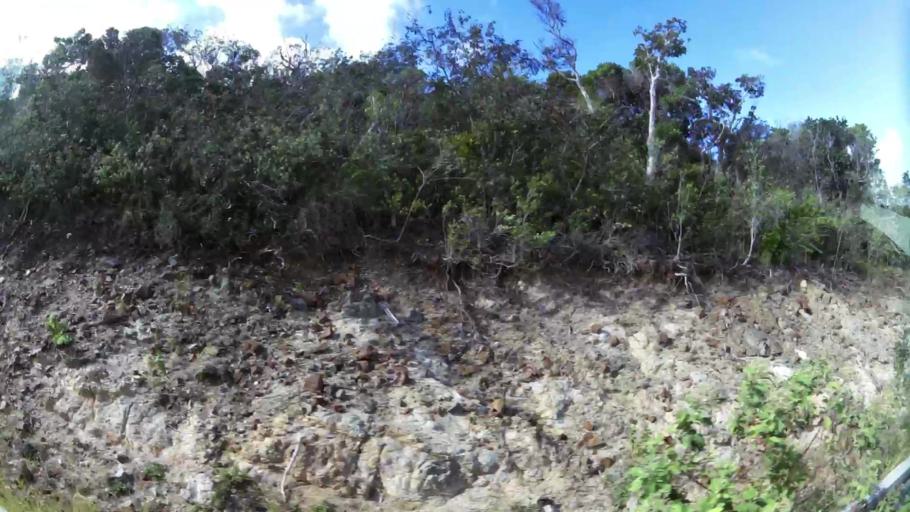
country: VG
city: Tortola
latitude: 18.4997
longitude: -64.4047
